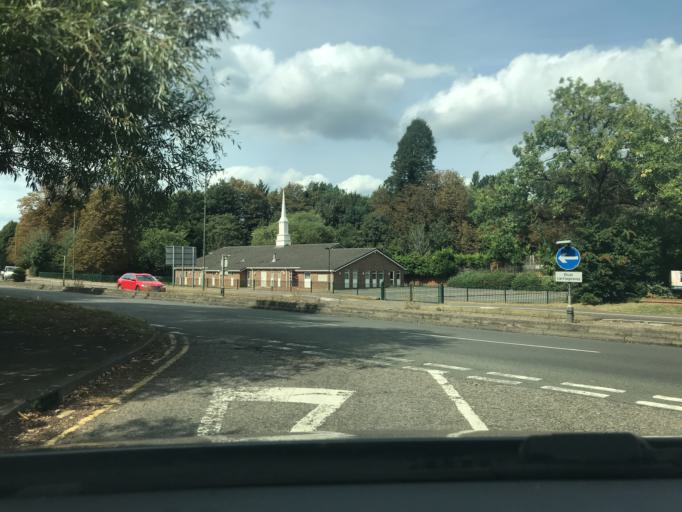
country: GB
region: England
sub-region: Surrey
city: Addlestone
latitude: 51.3735
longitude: -0.4764
